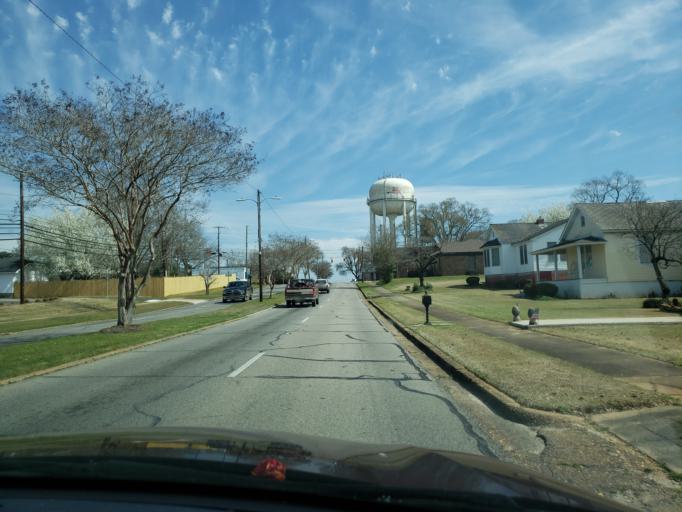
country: US
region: Alabama
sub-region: Elmore County
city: Tallassee
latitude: 32.5363
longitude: -85.8961
